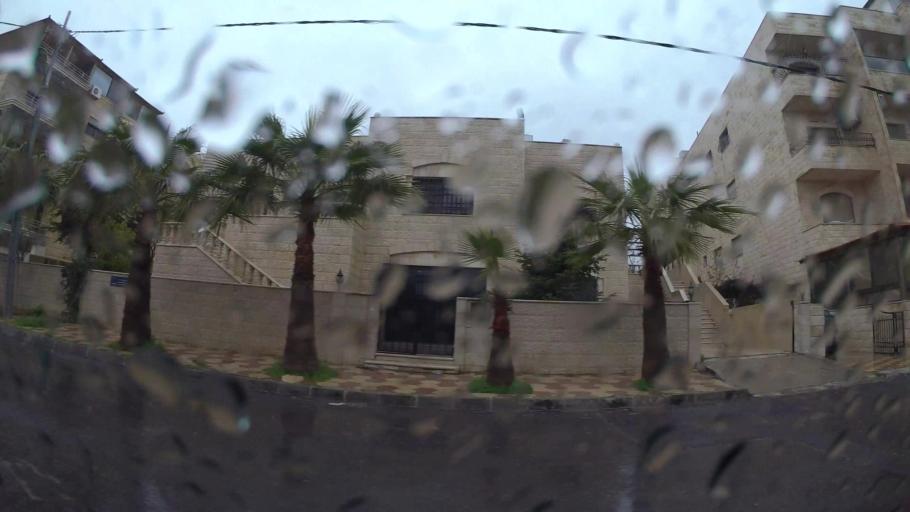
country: JO
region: Amman
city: Al Jubayhah
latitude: 32.0264
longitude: 35.8864
